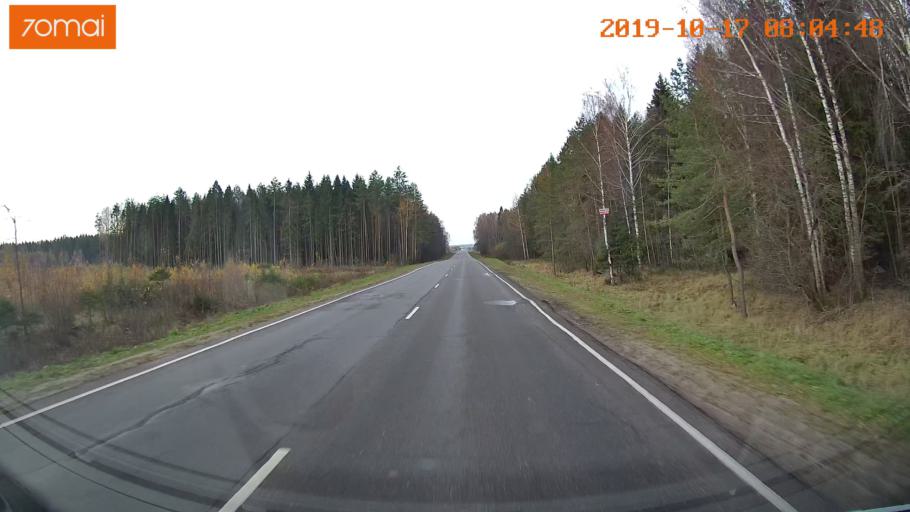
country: RU
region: Vladimir
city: Belaya Rechka
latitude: 56.3415
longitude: 39.4281
